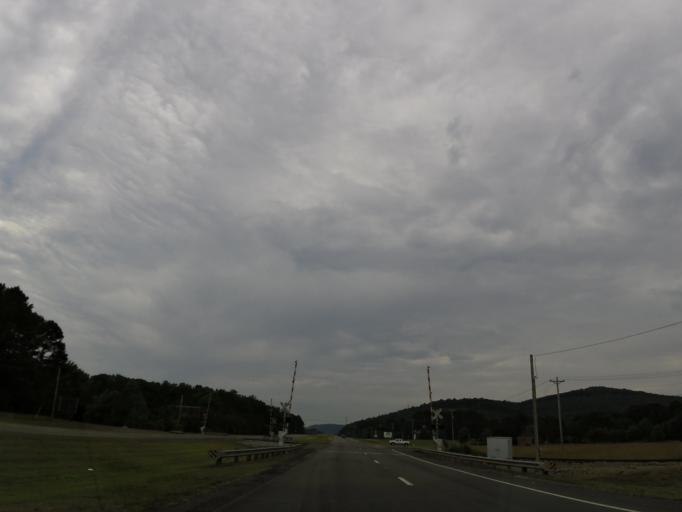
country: US
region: Alabama
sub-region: Jackson County
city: Scottsboro
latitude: 34.6390
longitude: -86.0524
